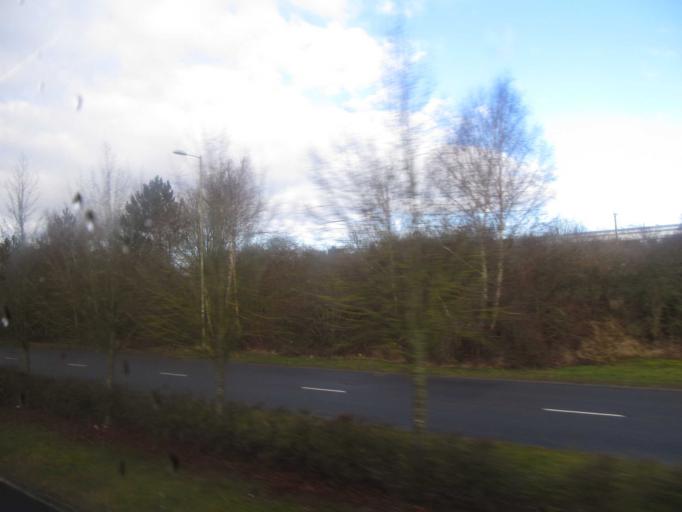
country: GB
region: England
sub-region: Hampshire
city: Basingstoke
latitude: 51.2663
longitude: -1.1019
